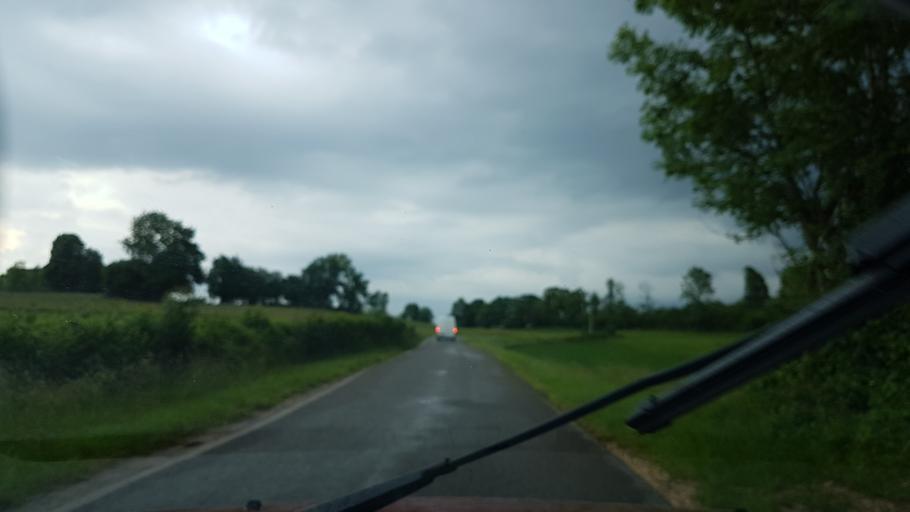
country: FR
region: Franche-Comte
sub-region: Departement du Jura
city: Clairvaux-les-Lacs
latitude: 46.5368
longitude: 5.7415
